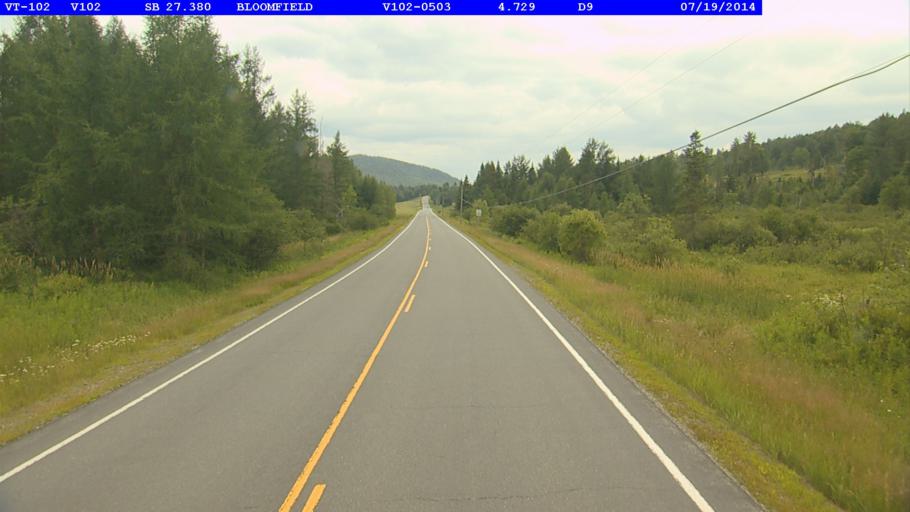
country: US
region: New Hampshire
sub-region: Coos County
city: Colebrook
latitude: 44.7991
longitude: -71.5752
